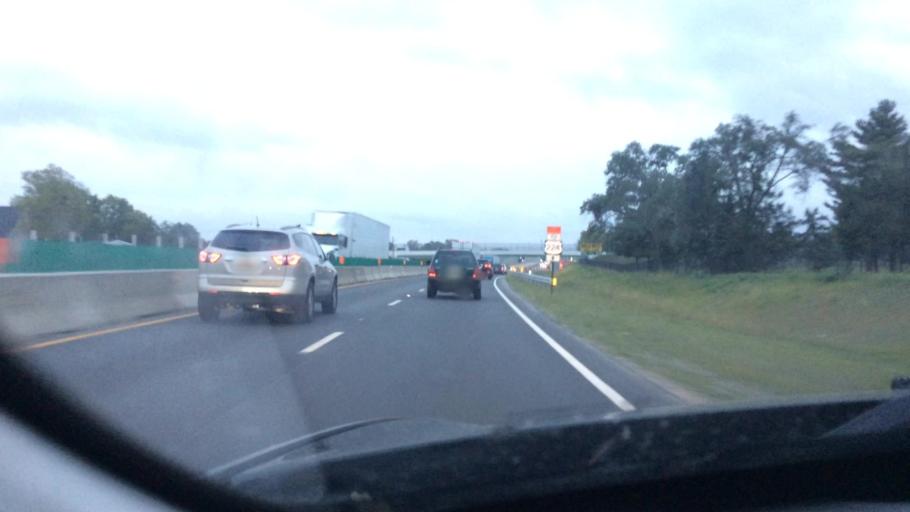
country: US
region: Ohio
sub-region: Hancock County
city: Findlay
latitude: 41.0760
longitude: -83.6605
